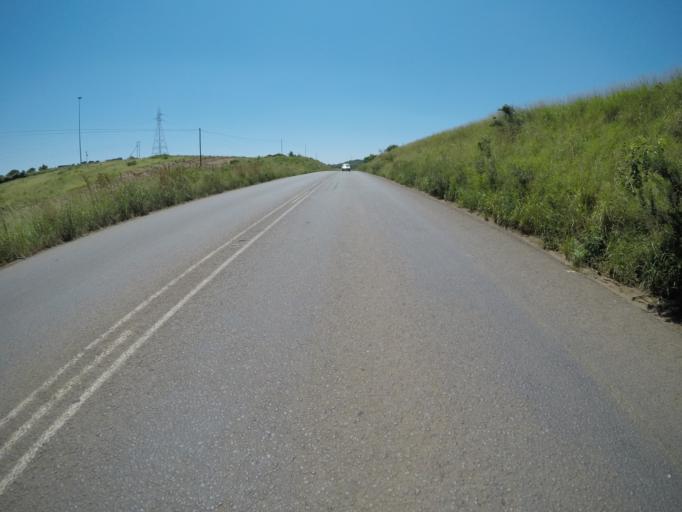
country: ZA
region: KwaZulu-Natal
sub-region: uThungulu District Municipality
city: Empangeni
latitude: -28.7629
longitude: 31.8753
